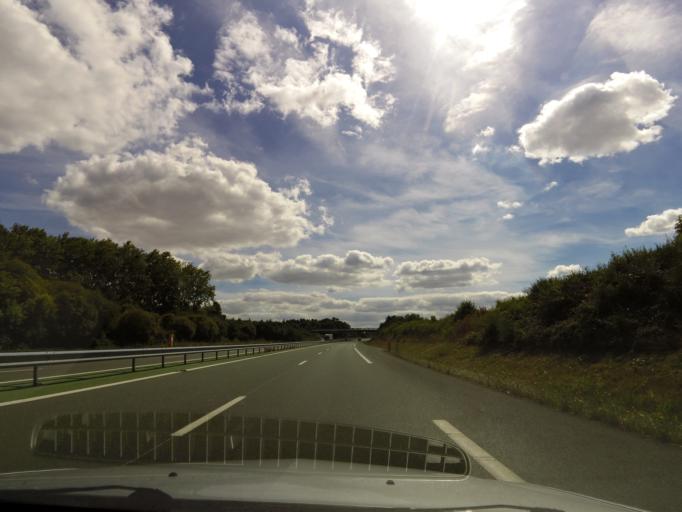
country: FR
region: Pays de la Loire
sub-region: Departement de la Vendee
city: Les Essarts
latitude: 46.7445
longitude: -1.2667
